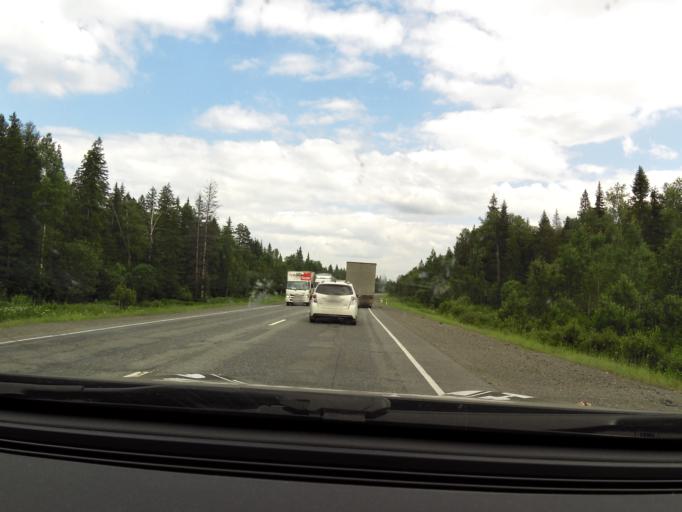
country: RU
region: Sverdlovsk
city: Atig
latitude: 56.8208
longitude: 59.3399
